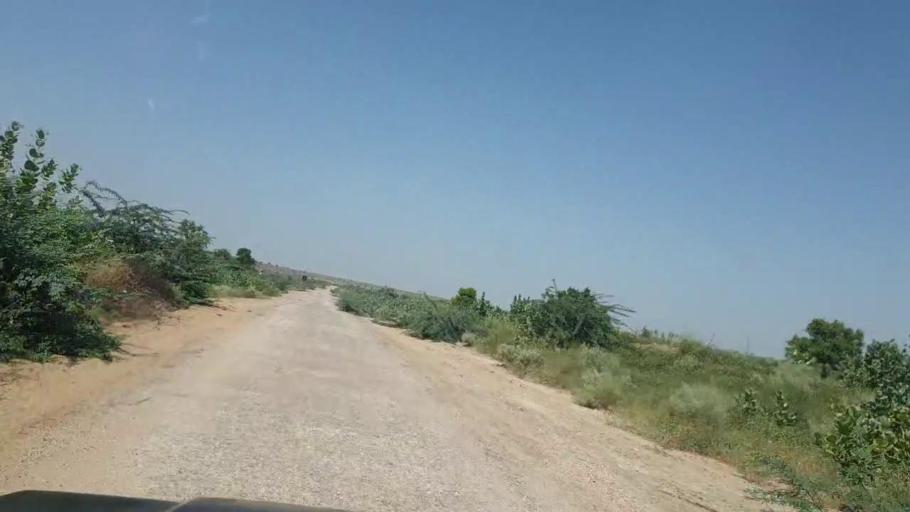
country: PK
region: Sindh
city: Chor
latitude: 25.3673
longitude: 70.3218
